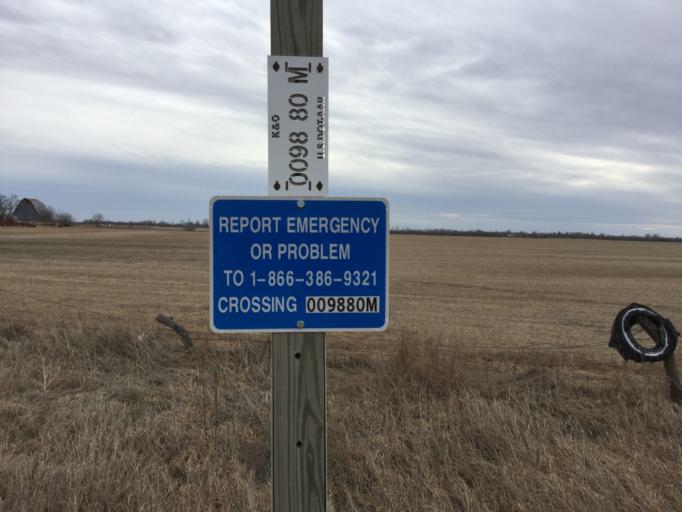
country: US
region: Kansas
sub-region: Rice County
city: Sterling
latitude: 38.2168
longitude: -98.2362
